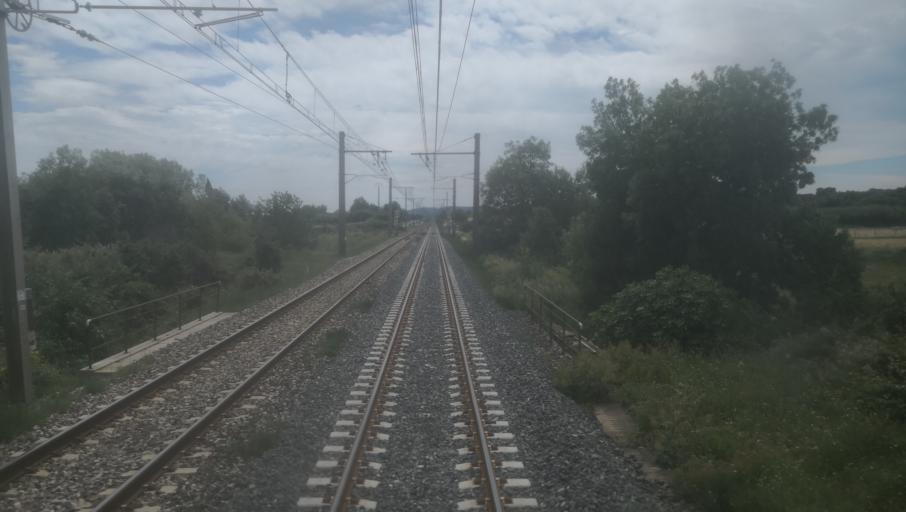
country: FR
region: Languedoc-Roussillon
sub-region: Departement de l'Herault
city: Mireval
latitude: 43.5235
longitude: 3.8302
